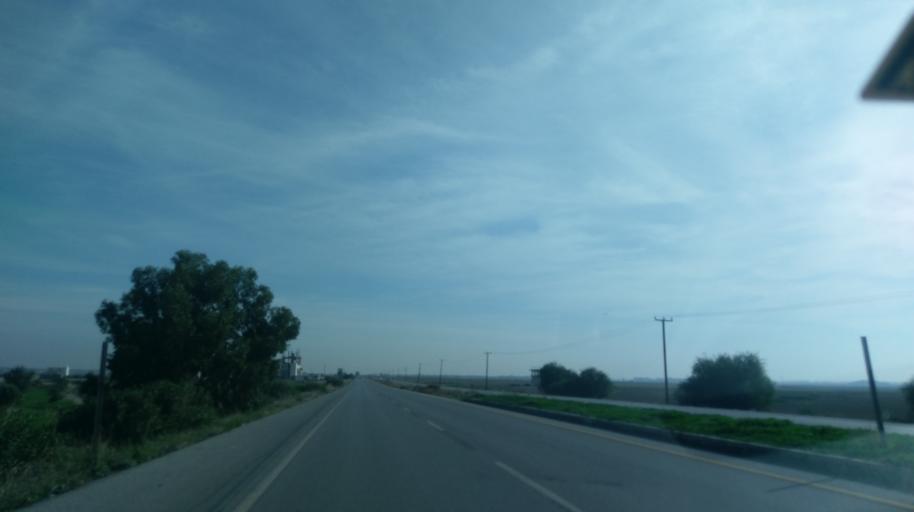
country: CY
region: Larnaka
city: Athienou
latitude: 35.2119
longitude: 33.5302
